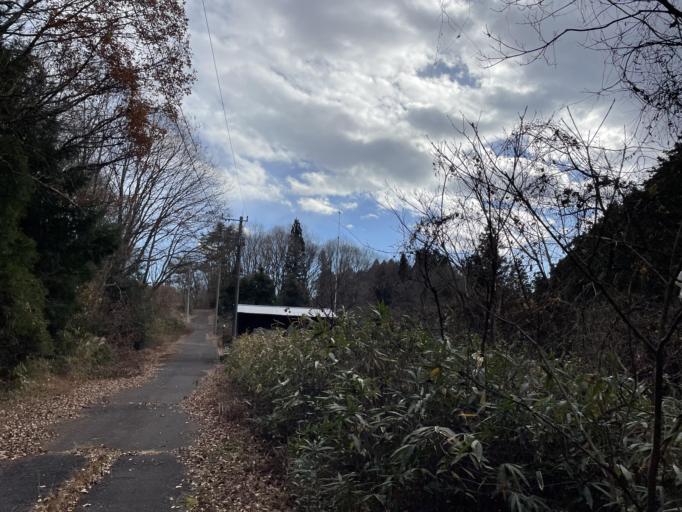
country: JP
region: Tochigi
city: Imaichi
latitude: 36.6968
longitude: 139.7134
